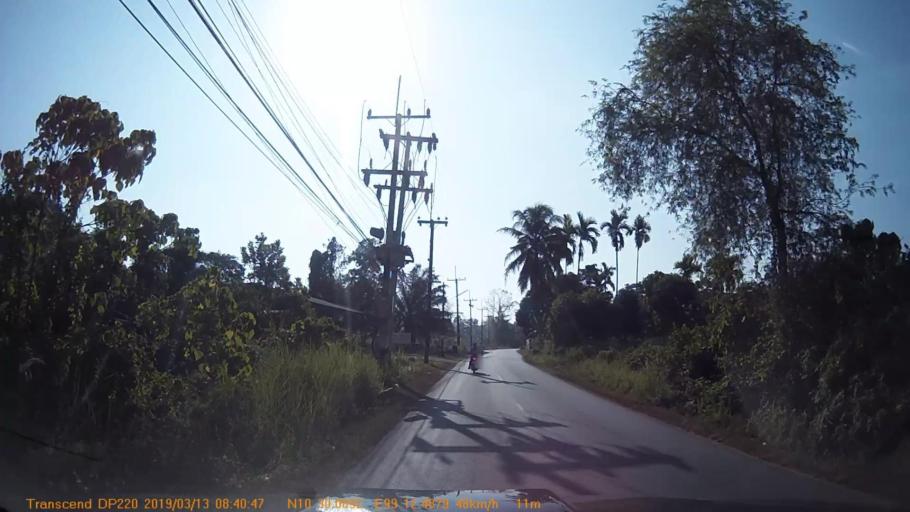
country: TH
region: Chumphon
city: Chumphon
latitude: 10.5014
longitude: 99.2083
